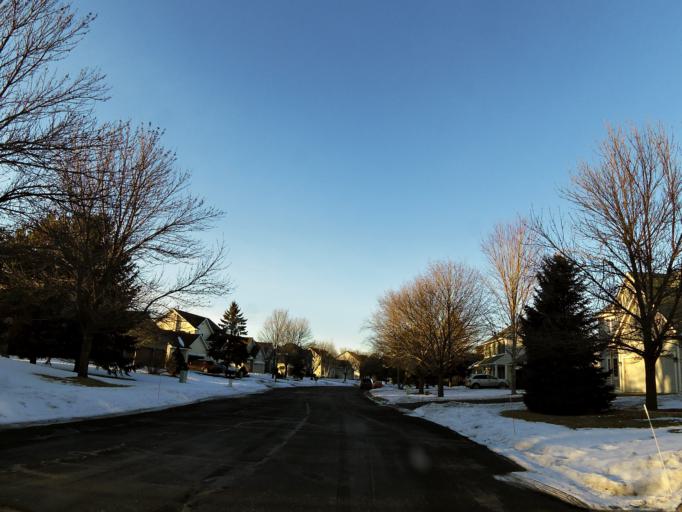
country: US
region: Minnesota
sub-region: Washington County
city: Woodbury
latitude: 44.8921
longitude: -92.8991
